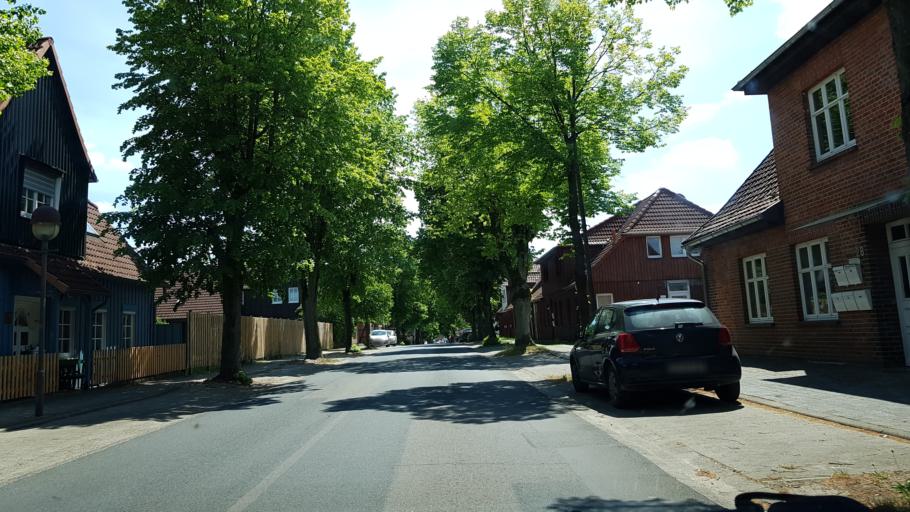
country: DE
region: Lower Saxony
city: Eschede
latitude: 52.7380
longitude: 10.2322
